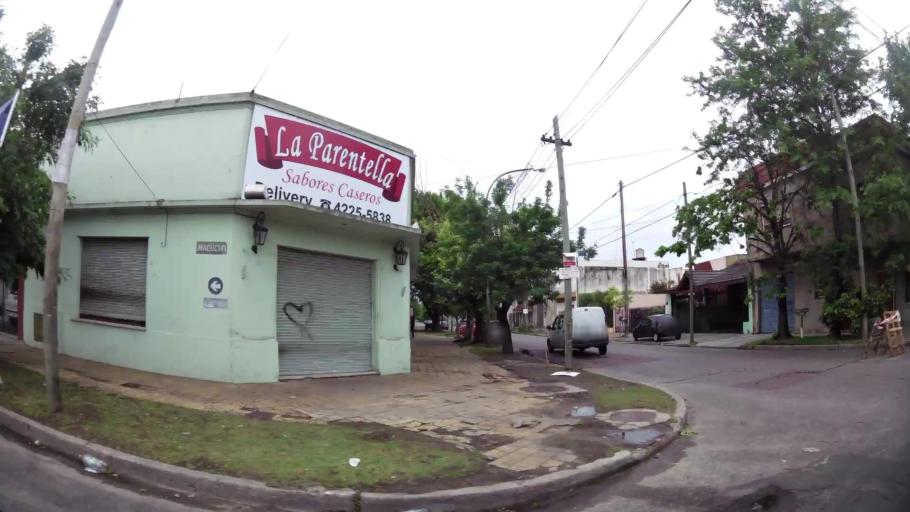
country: AR
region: Buenos Aires
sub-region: Partido de Lanus
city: Lanus
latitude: -34.7013
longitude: -58.3793
